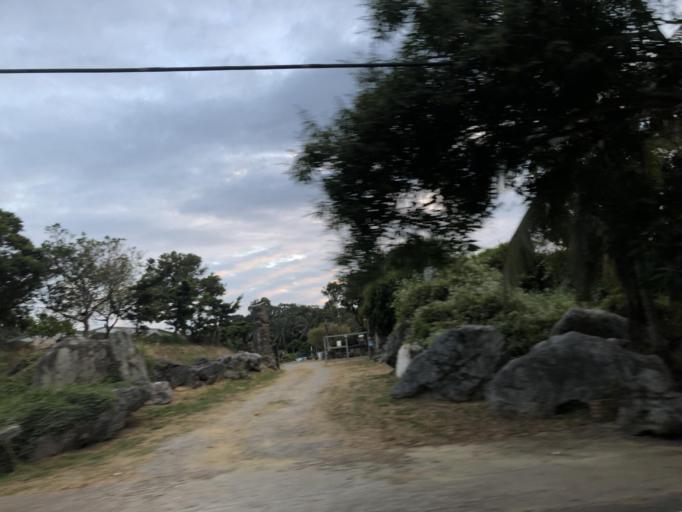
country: TW
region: Taiwan
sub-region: Tainan
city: Tainan
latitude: 23.0249
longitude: 120.3485
